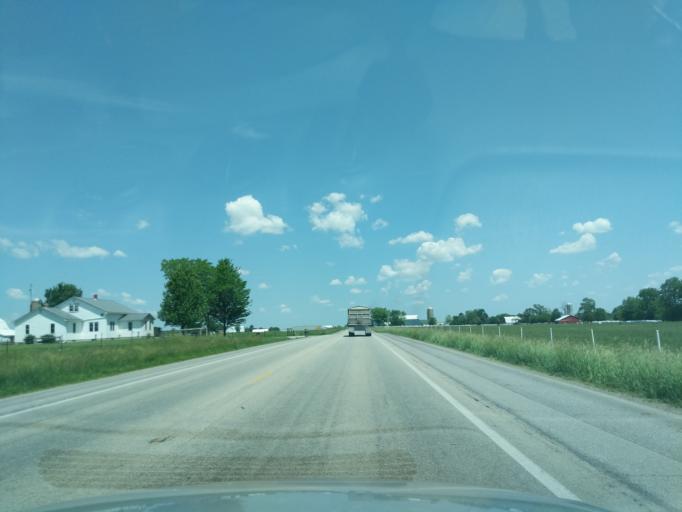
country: US
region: Indiana
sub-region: LaGrange County
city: Topeka
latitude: 41.5758
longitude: -85.5786
